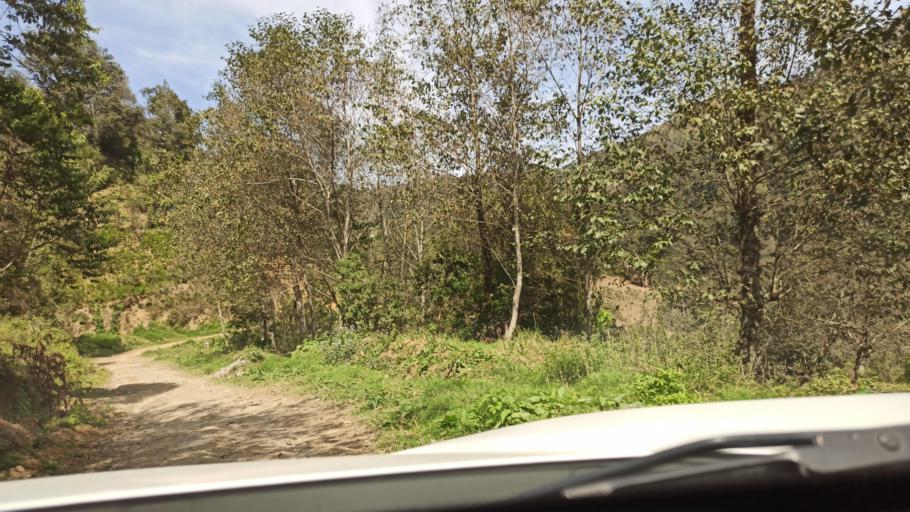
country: MX
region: Veracruz
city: Xocotla
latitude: 18.9869
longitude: -97.0990
